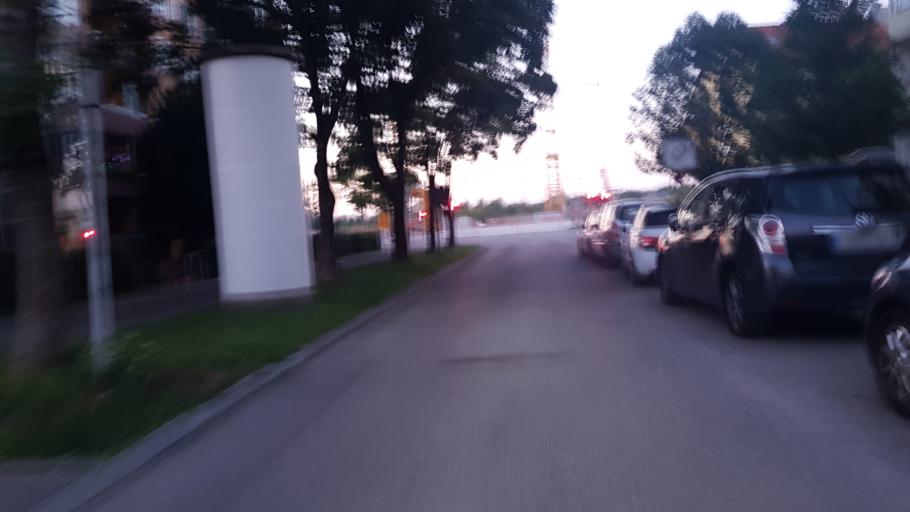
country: DE
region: Bavaria
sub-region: Upper Bavaria
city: Pasing
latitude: 48.1432
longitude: 11.4932
